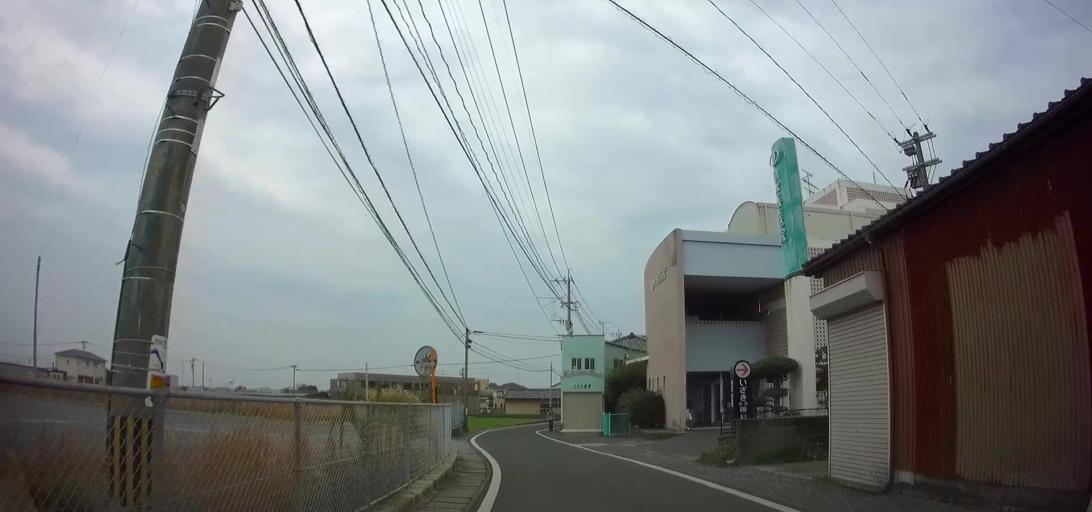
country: JP
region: Nagasaki
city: Shimabara
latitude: 32.6621
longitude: 130.2998
